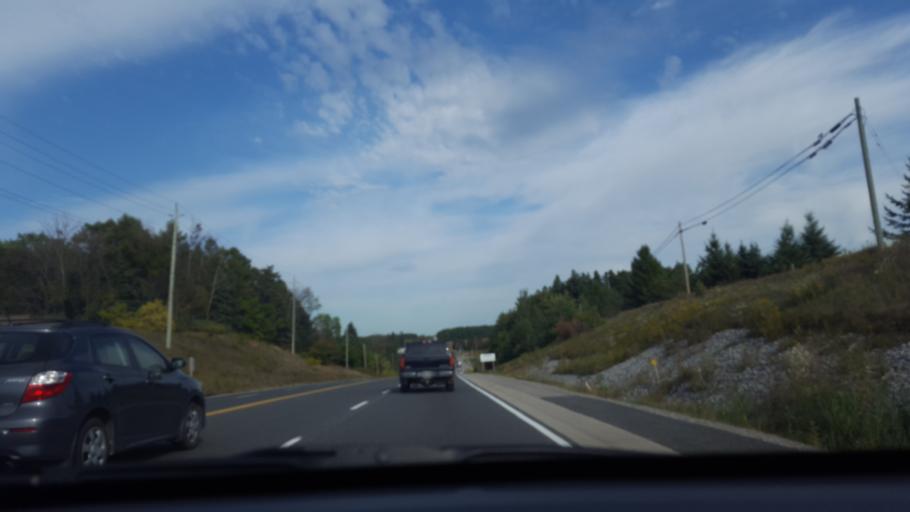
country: CA
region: Ontario
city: Vaughan
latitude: 43.9215
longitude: -79.5611
